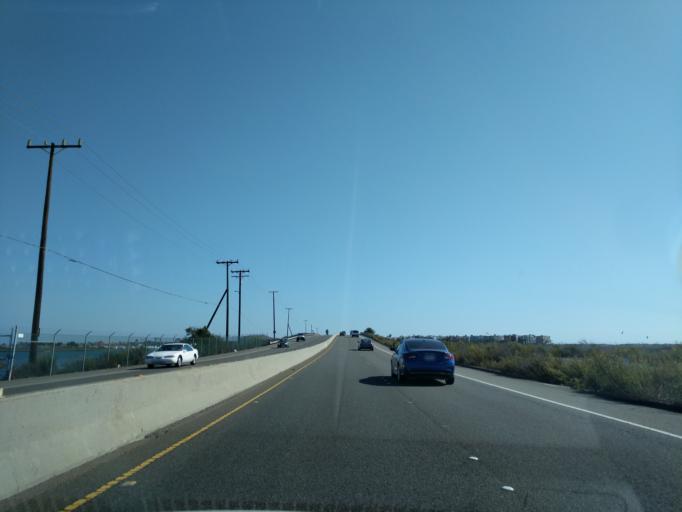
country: US
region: California
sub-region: Orange County
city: Seal Beach
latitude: 33.7346
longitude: -118.0859
